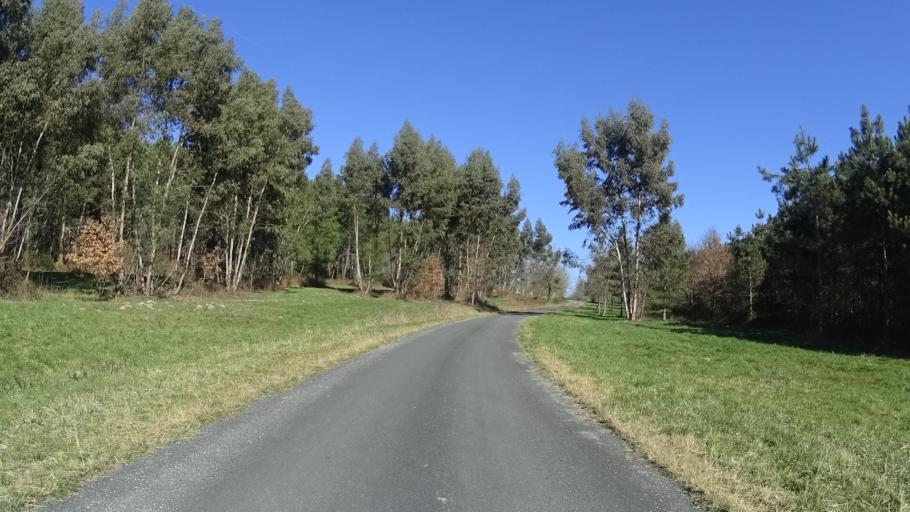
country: FR
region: Aquitaine
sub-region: Departement de la Dordogne
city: Saint-Aulaye
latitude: 45.1240
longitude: 0.2136
